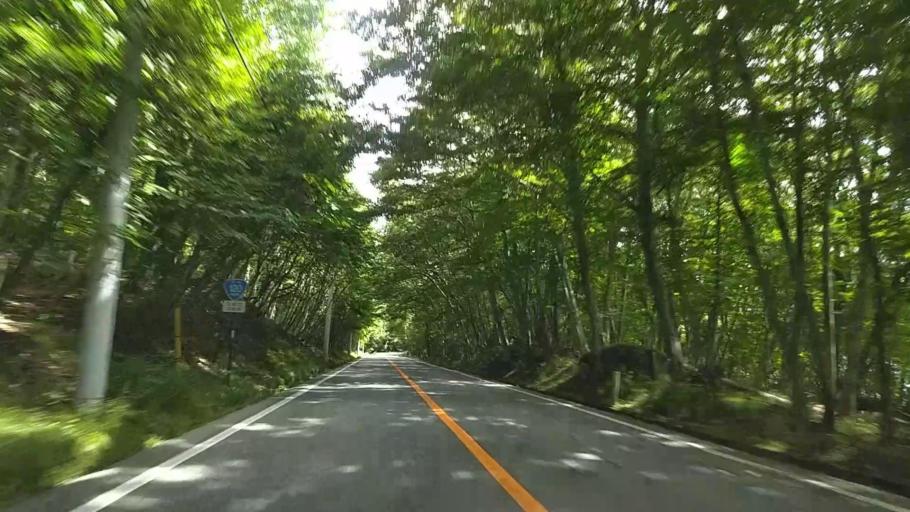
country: JP
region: Tochigi
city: Nikko
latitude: 36.7489
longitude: 139.4654
